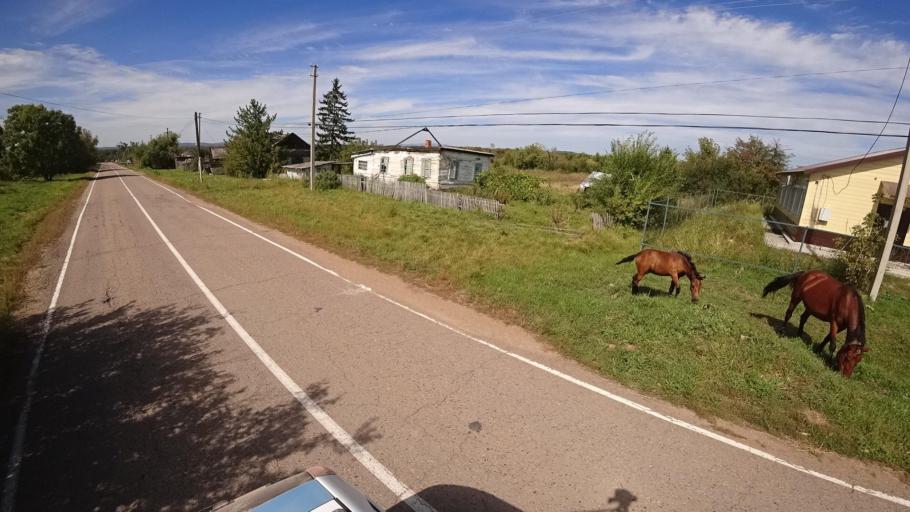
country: RU
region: Primorskiy
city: Yakovlevka
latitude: 44.4335
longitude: 133.5621
